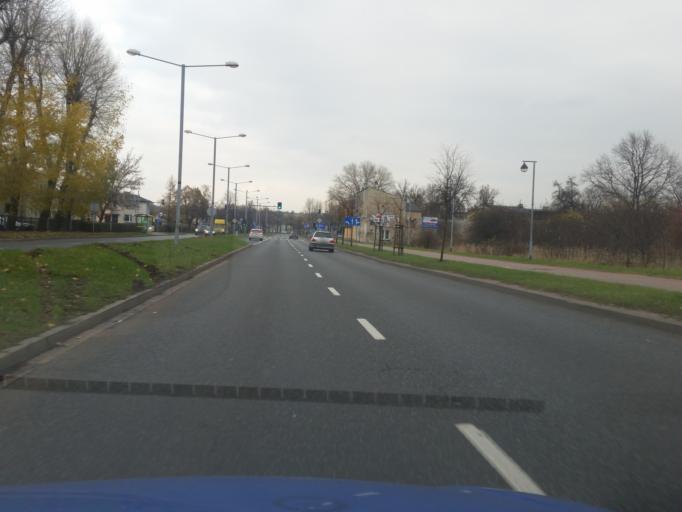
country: PL
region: Silesian Voivodeship
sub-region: Czestochowa
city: Czestochowa
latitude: 50.8049
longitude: 19.1381
